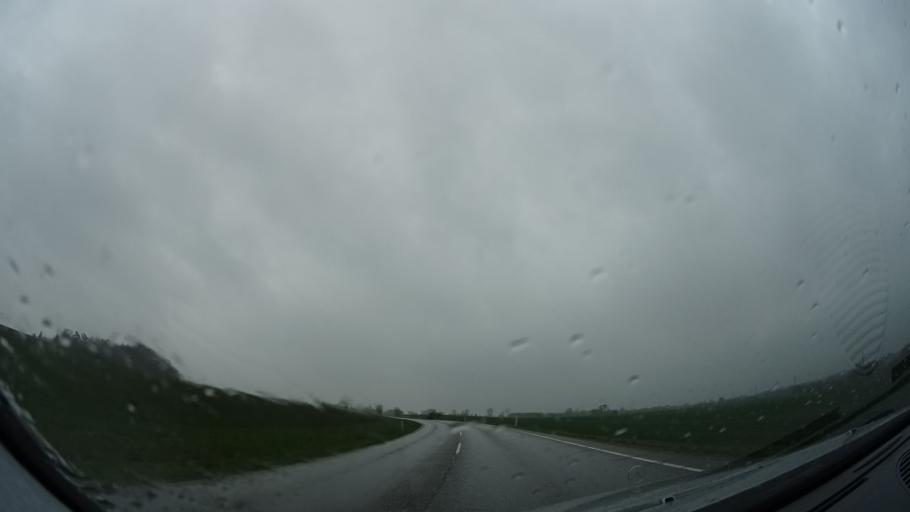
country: DK
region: Zealand
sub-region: Holbaek Kommune
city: Holbaek
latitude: 55.7559
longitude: 11.6240
